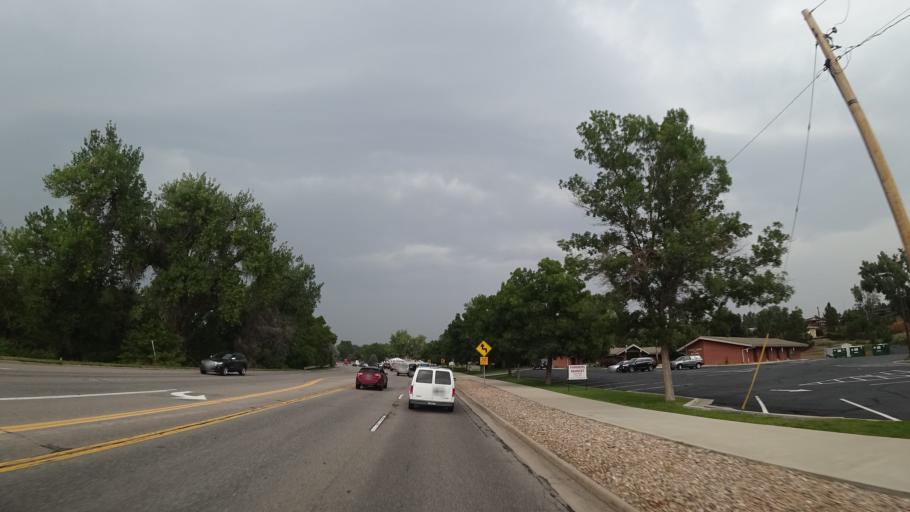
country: US
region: Colorado
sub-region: Arapahoe County
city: Southglenn
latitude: 39.6011
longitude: -104.9581
